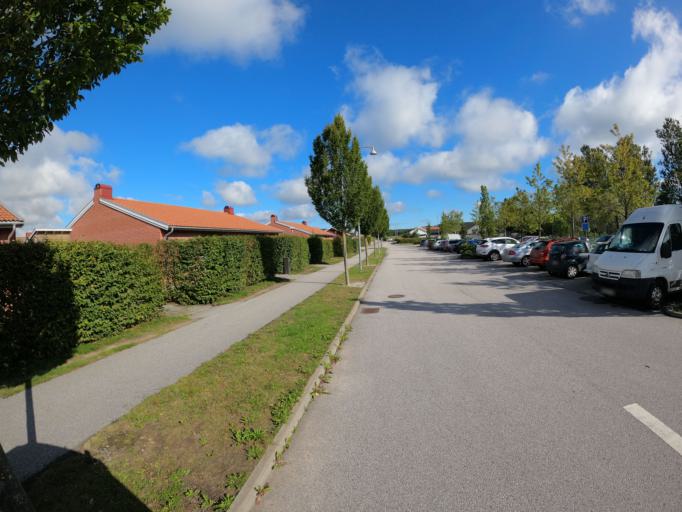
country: SE
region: Skane
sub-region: Lunds Kommun
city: Genarp
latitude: 55.6023
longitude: 13.4063
